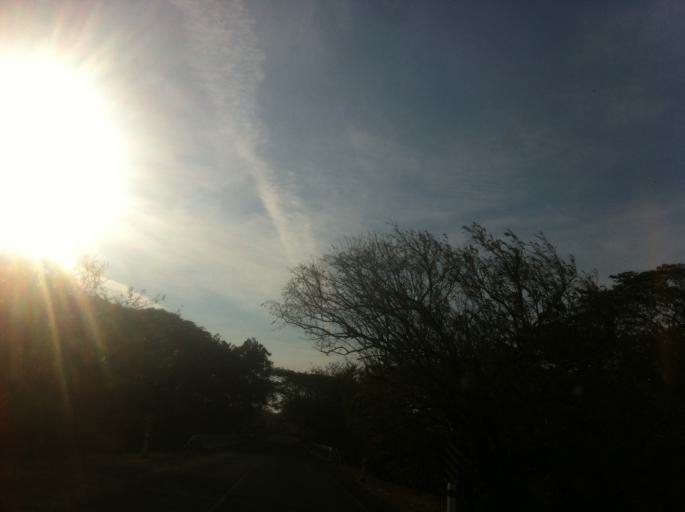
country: NI
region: Rivas
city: Cardenas
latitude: 11.2807
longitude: -85.6692
